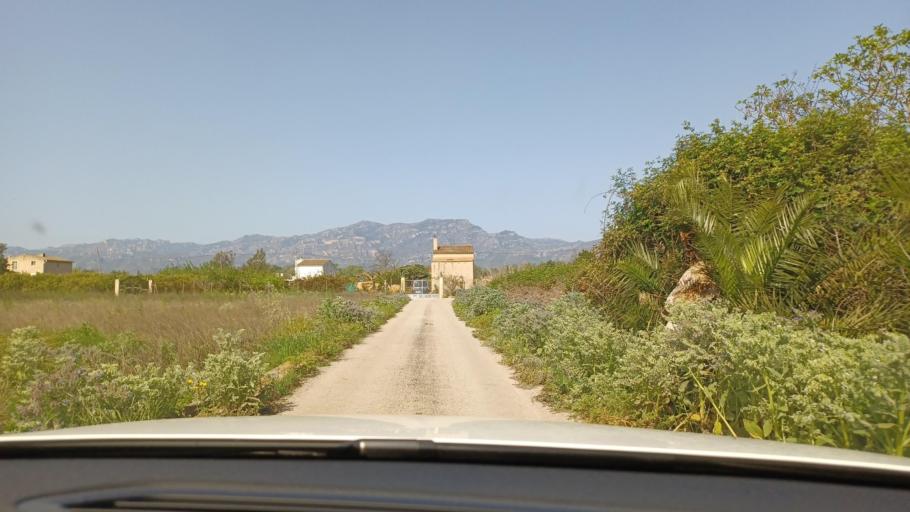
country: ES
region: Catalonia
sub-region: Provincia de Tarragona
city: Tortosa
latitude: 40.7927
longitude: 0.5130
